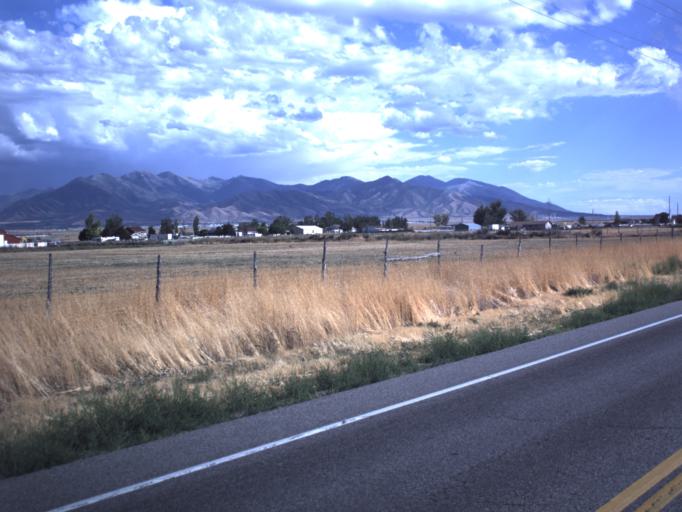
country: US
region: Utah
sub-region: Tooele County
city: Grantsville
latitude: 40.5973
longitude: -112.4260
